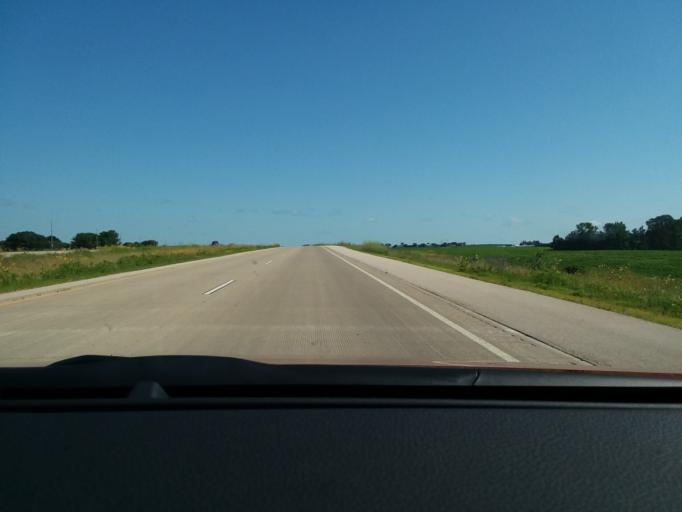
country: US
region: Wisconsin
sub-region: Dane County
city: De Forest
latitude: 43.2349
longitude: -89.3227
